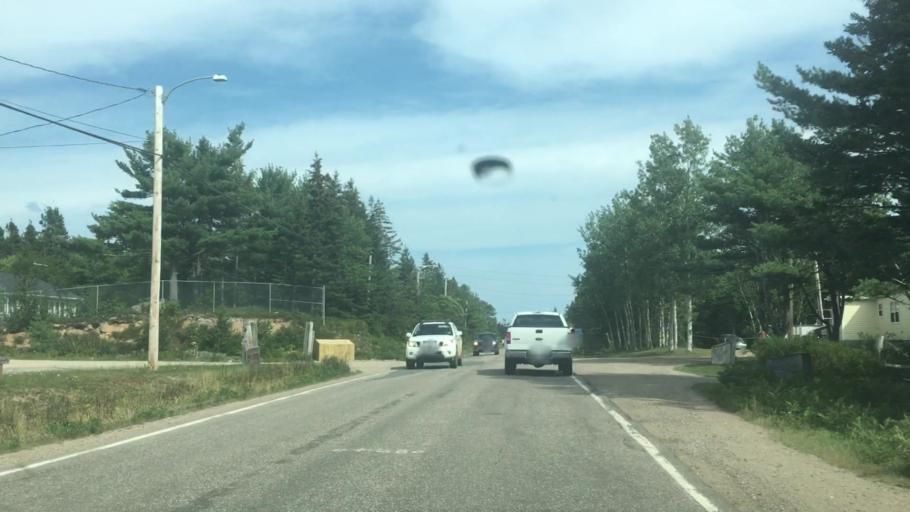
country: CA
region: Nova Scotia
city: Sydney Mines
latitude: 46.6900
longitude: -60.3859
